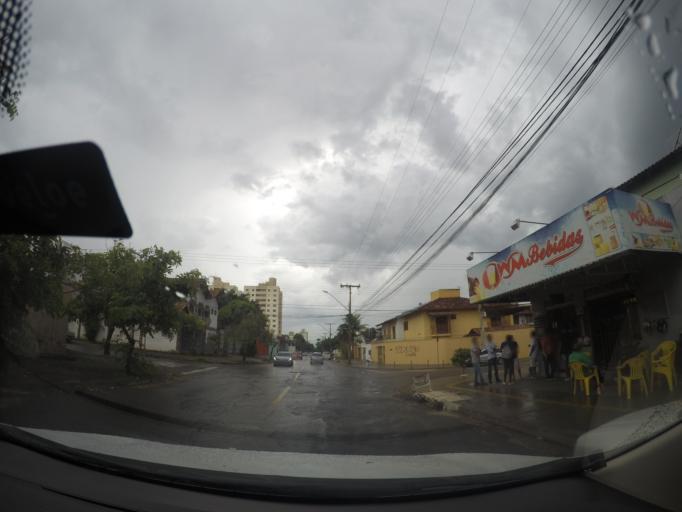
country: BR
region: Goias
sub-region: Goiania
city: Goiania
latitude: -16.7121
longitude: -49.2800
